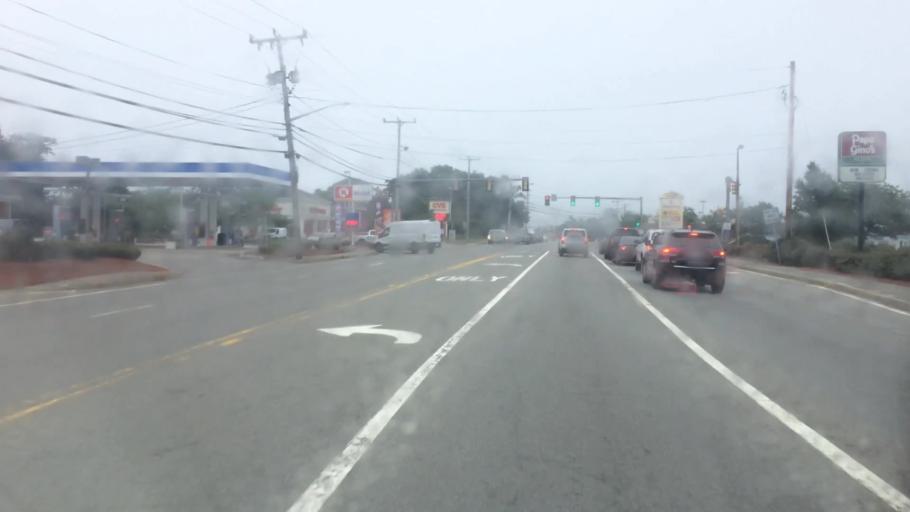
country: US
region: Massachusetts
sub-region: Plymouth County
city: Onset
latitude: 41.7598
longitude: -70.6676
